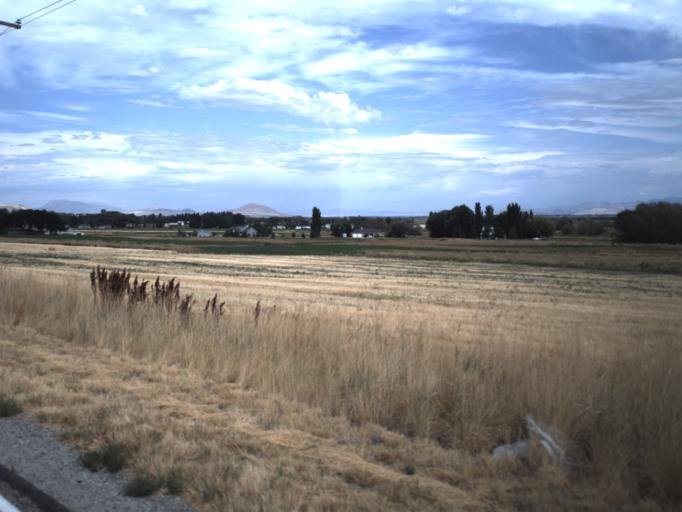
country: US
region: Utah
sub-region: Cache County
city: Mendon
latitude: 41.6897
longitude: -111.9685
